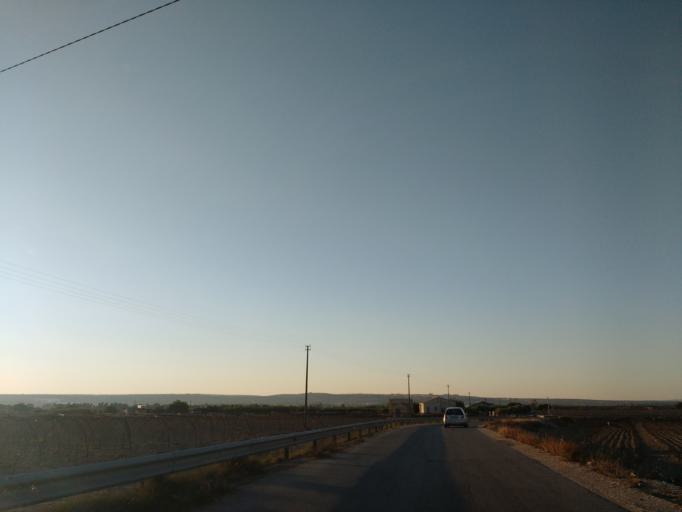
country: IT
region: Sicily
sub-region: Ragusa
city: Ispica
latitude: 36.7337
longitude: 14.9274
